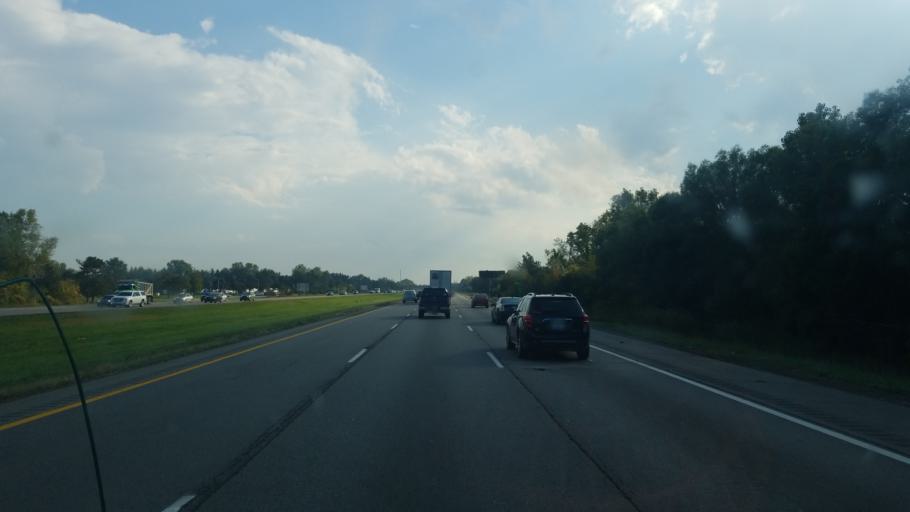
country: US
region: Michigan
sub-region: Wayne County
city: Canton
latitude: 42.3037
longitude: -83.4430
